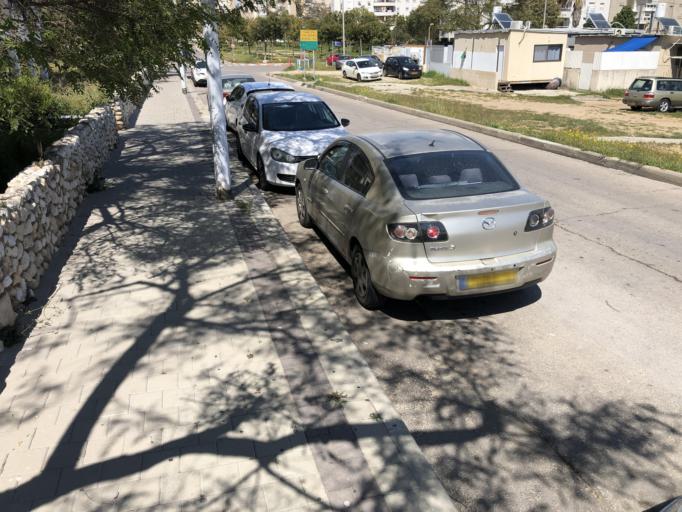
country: IL
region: Tel Aviv
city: Bat Yam
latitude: 32.0061
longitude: 34.7565
